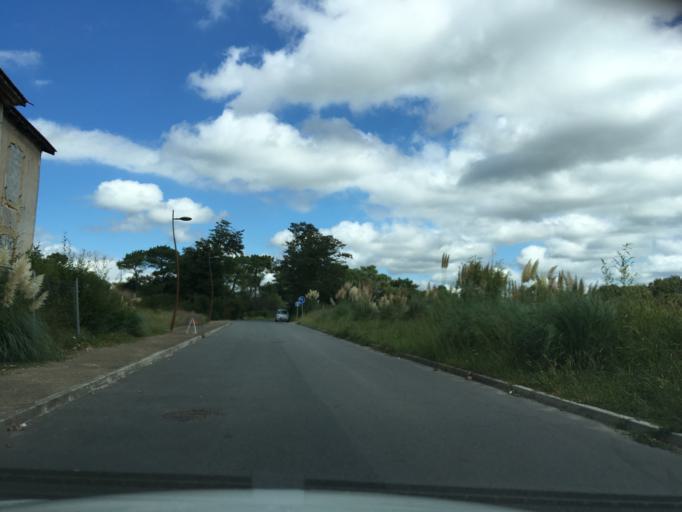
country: FR
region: Aquitaine
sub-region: Departement des Pyrenees-Atlantiques
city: Mouguerre
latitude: 43.5065
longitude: -1.4303
